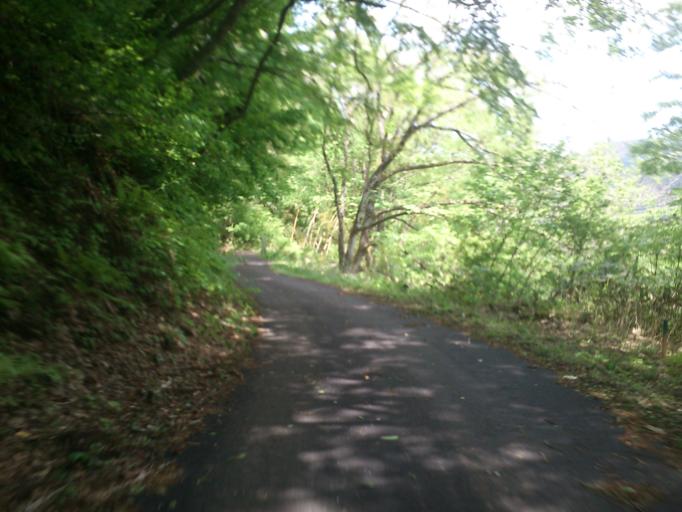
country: JP
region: Kyoto
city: Miyazu
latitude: 35.6486
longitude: 135.1566
